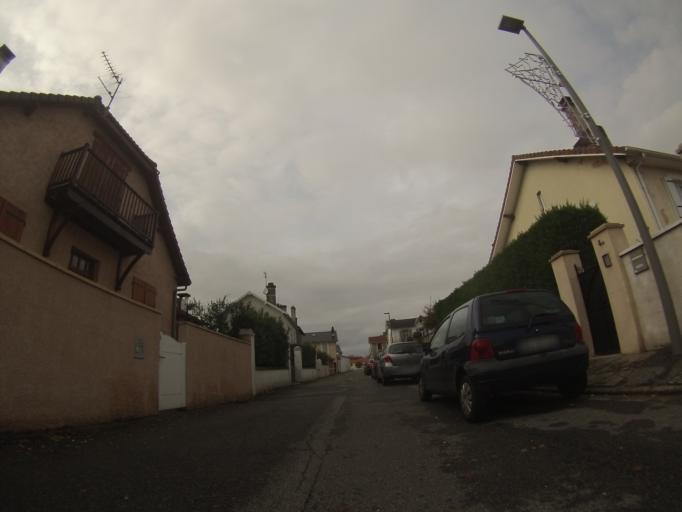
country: FR
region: Aquitaine
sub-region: Departement des Pyrenees-Atlantiques
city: Jurancon
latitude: 43.2884
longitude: -0.3862
